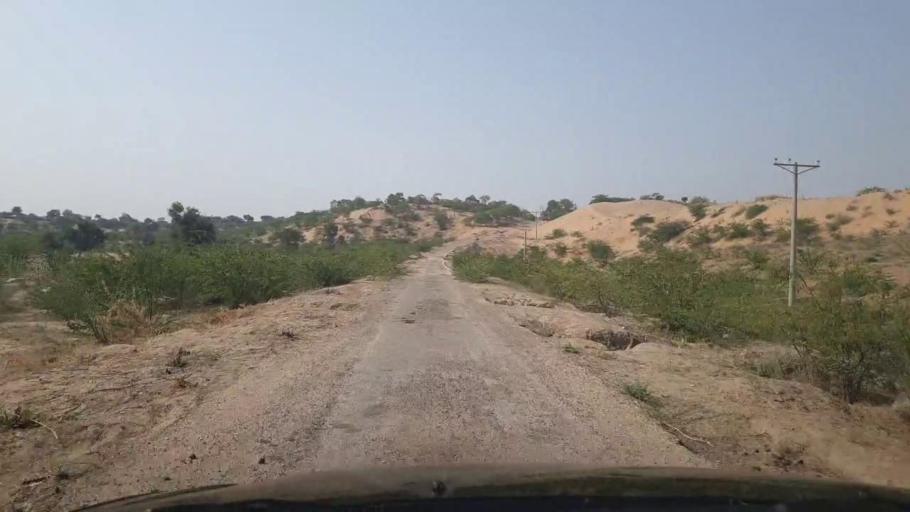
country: PK
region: Sindh
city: Islamkot
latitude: 25.0013
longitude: 70.2076
